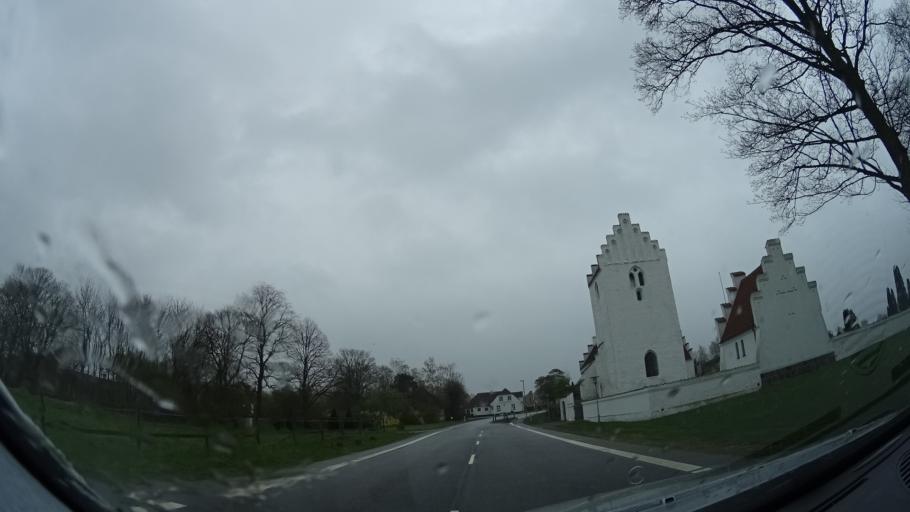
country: DK
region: Zealand
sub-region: Holbaek Kommune
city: Holbaek
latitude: 55.7158
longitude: 11.6153
